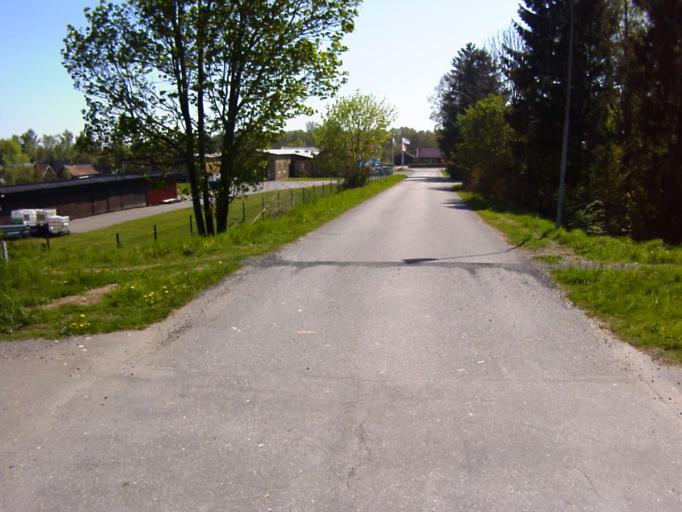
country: SE
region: Skane
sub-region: Kristianstads Kommun
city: Degeberga
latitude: 55.8999
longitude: 14.0964
